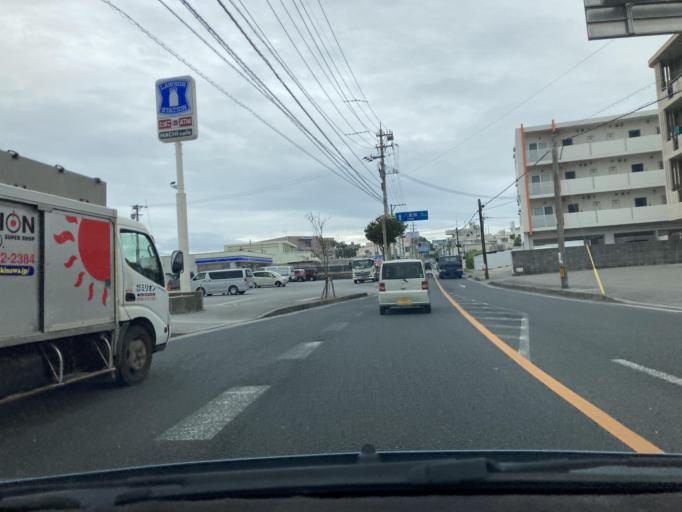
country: JP
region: Okinawa
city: Tomigusuku
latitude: 26.1784
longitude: 127.7182
